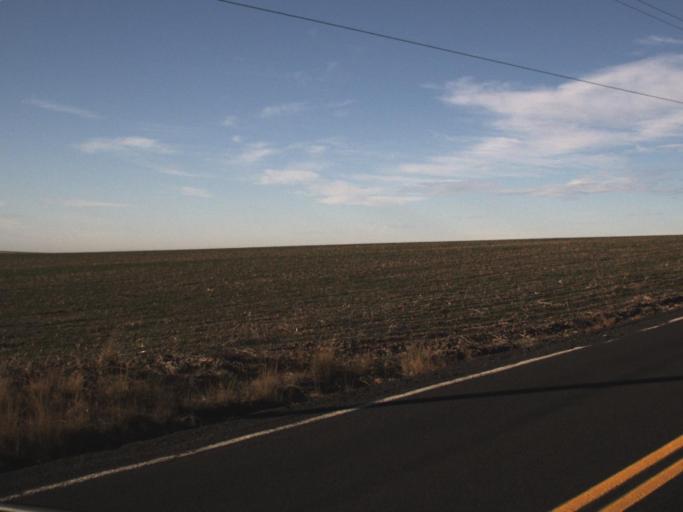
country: US
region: Washington
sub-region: Adams County
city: Ritzville
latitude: 47.1308
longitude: -118.6749
